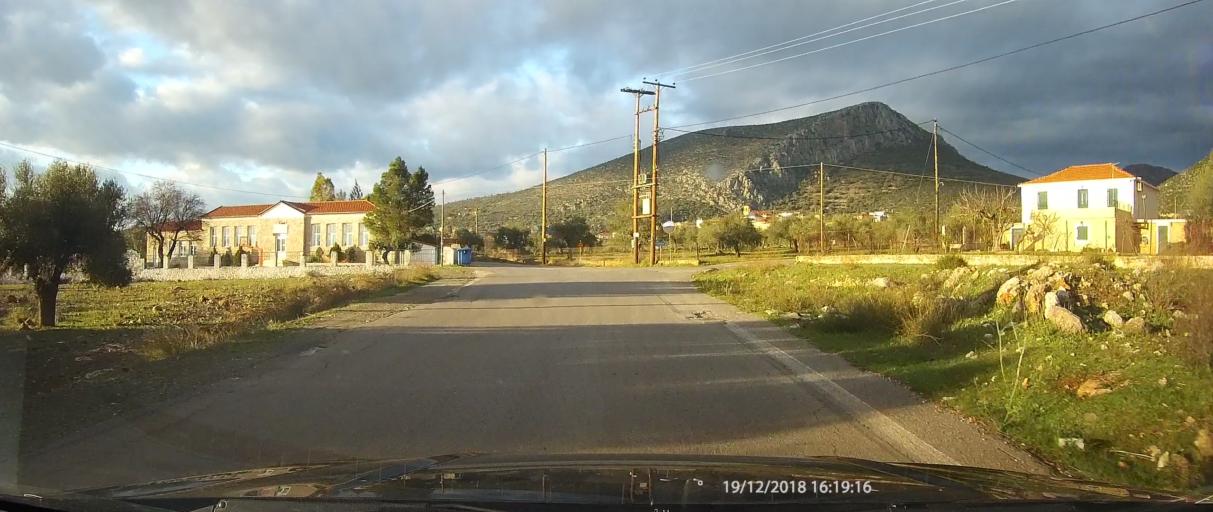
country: GR
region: Peloponnese
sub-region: Nomos Lakonias
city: Kato Glikovrisi
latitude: 36.9310
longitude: 22.8228
